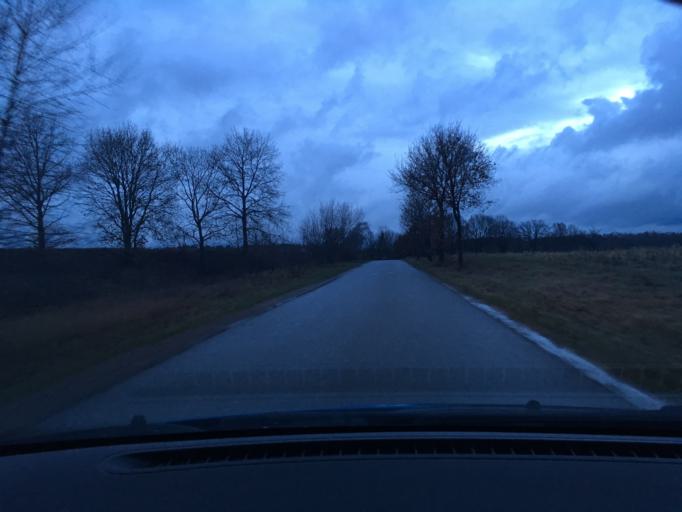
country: DE
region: Lower Saxony
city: Betzendorf
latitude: 53.1413
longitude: 10.3142
